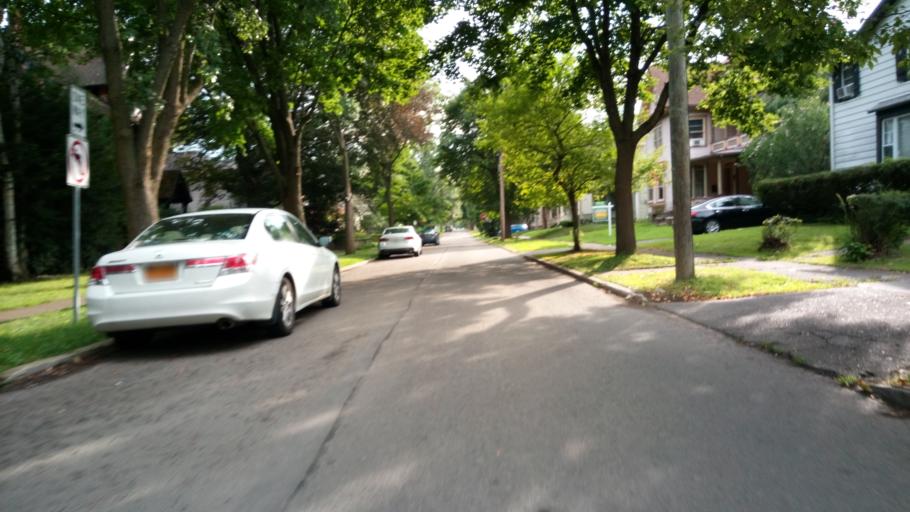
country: US
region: New York
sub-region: Chemung County
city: Elmira
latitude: 42.0867
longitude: -76.8157
